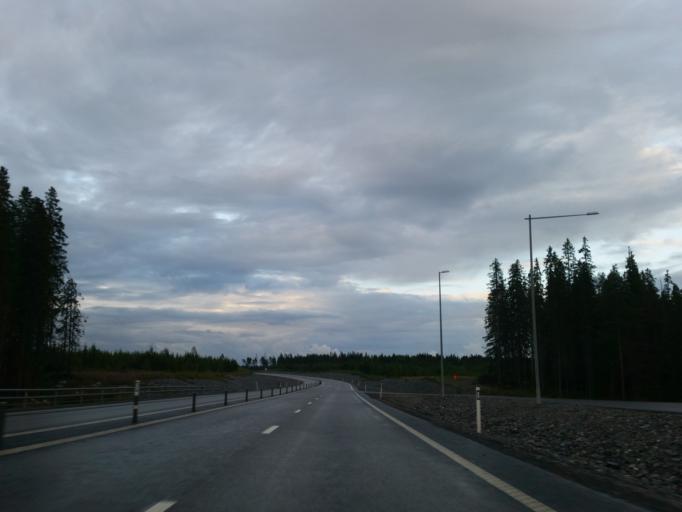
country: SE
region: Vaesterbotten
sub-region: Umea Kommun
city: Umea
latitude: 63.8561
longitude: 20.2583
